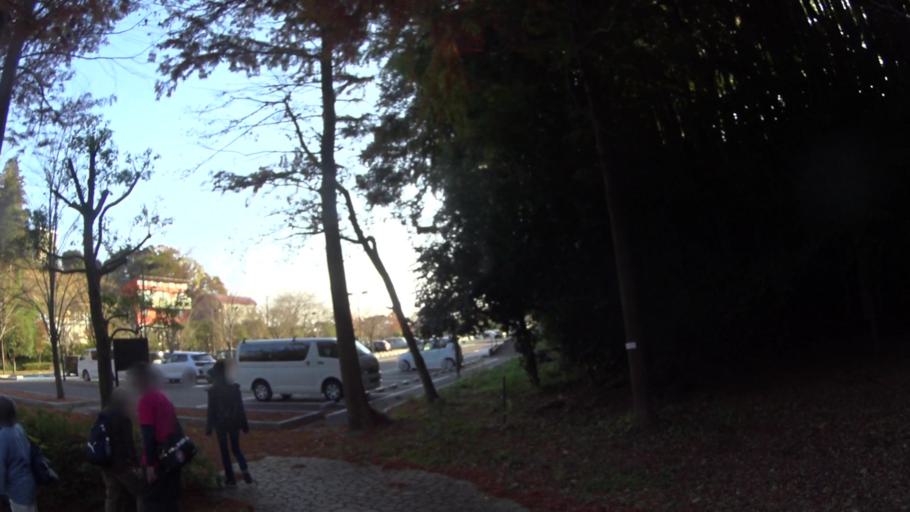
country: JP
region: Ibaraki
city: Mito-shi
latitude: 36.3744
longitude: 140.4599
